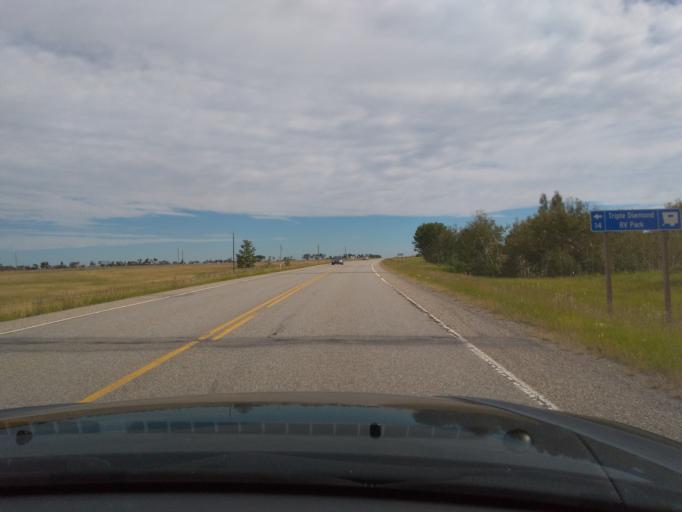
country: CA
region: Alberta
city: Cochrane
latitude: 51.3552
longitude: -114.4774
